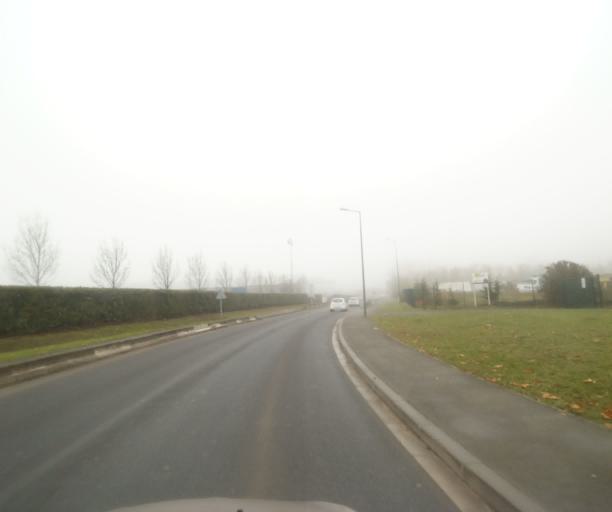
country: FR
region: Ile-de-France
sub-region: Departement de Seine-et-Marne
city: Villeparisis
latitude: 48.9357
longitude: 2.6019
